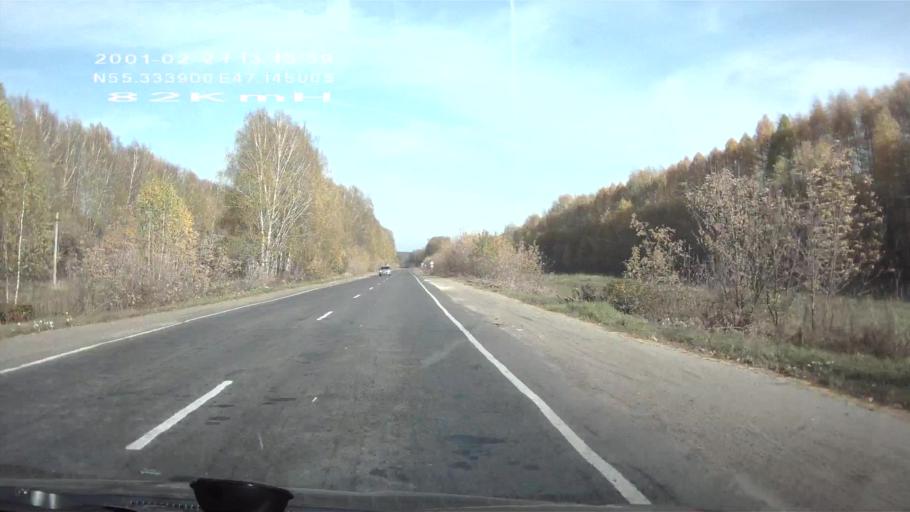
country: RU
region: Chuvashia
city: Ibresi
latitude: 55.3339
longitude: 47.1450
